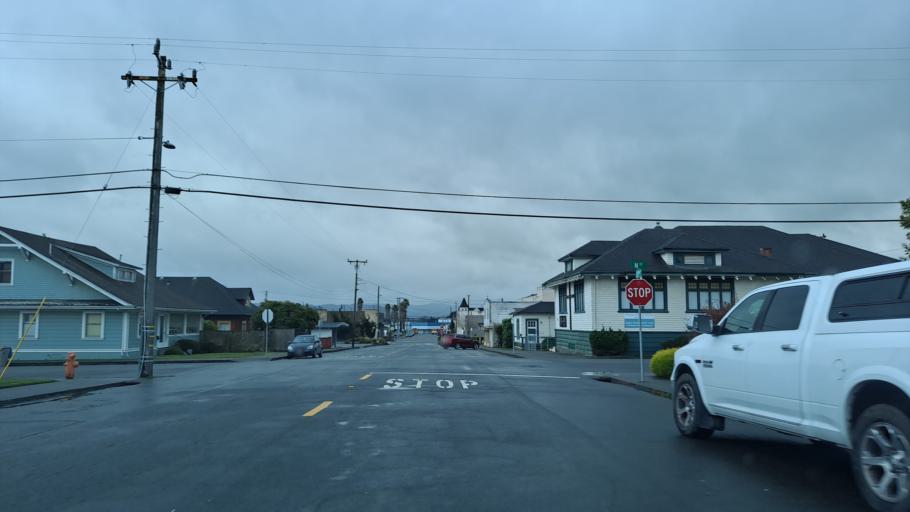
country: US
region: California
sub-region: Humboldt County
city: Fortuna
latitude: 40.5991
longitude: -124.1534
